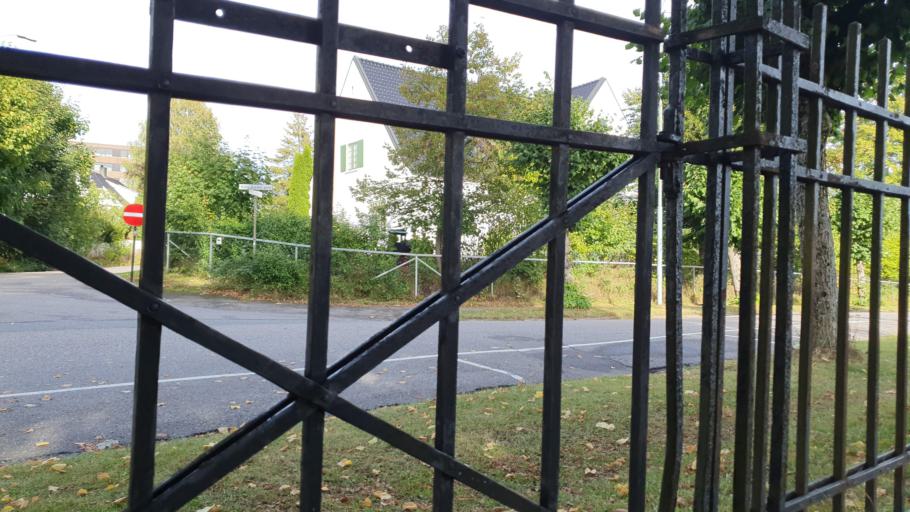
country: NO
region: Vestfold
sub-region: Tonsberg
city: Tonsberg
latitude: 59.2705
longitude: 10.4155
